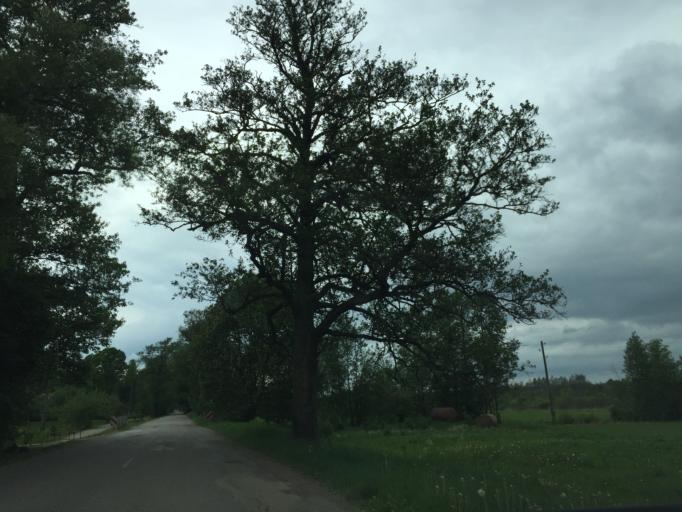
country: LV
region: Preilu Rajons
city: Preili
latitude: 56.0719
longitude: 26.7439
